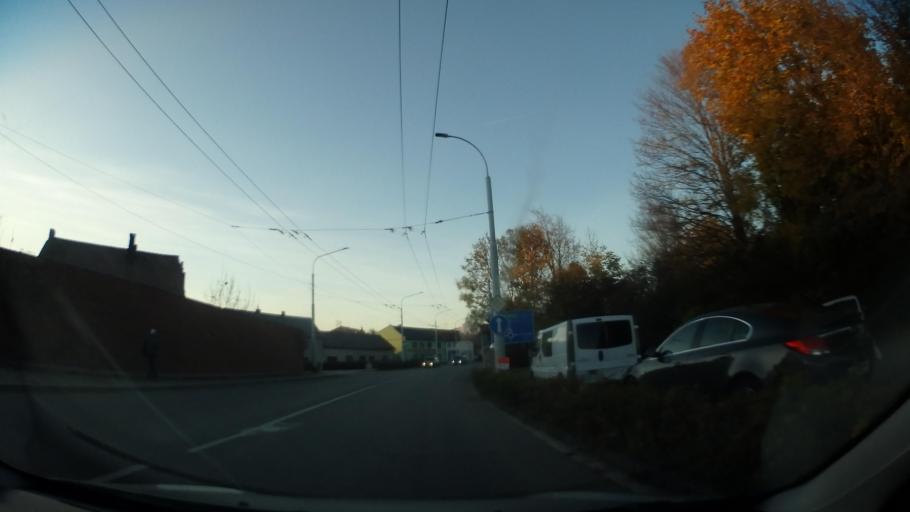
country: CZ
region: Pardubicky
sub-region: Okres Pardubice
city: Lazne Bohdanec
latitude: 50.0734
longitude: 15.6815
